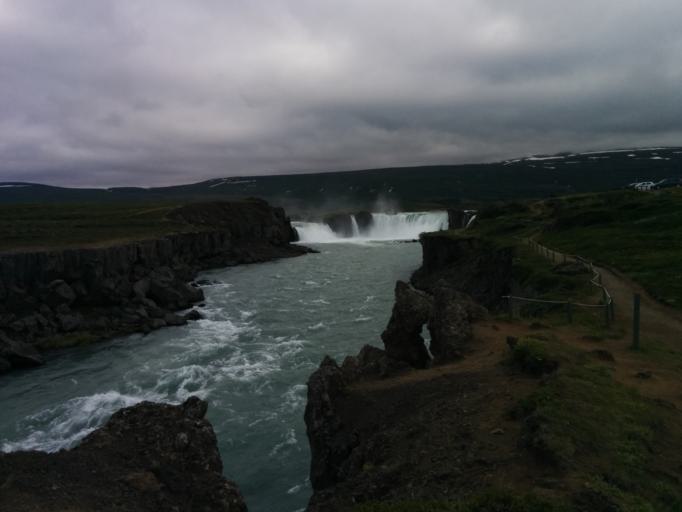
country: IS
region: Northeast
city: Laugar
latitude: 65.6846
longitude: -17.5461
